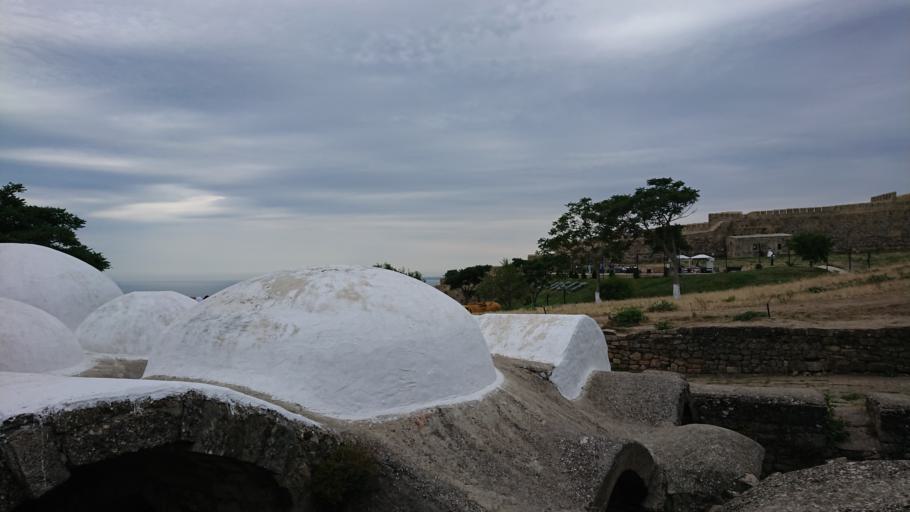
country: RU
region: Dagestan
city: Derbent
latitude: 42.0531
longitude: 48.2738
